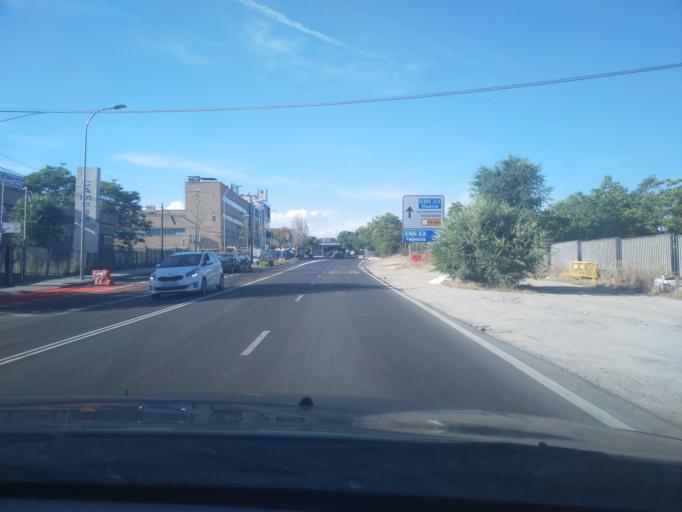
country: ES
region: Madrid
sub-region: Provincia de Madrid
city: Vicalvaro
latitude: 40.3883
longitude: -3.6230
